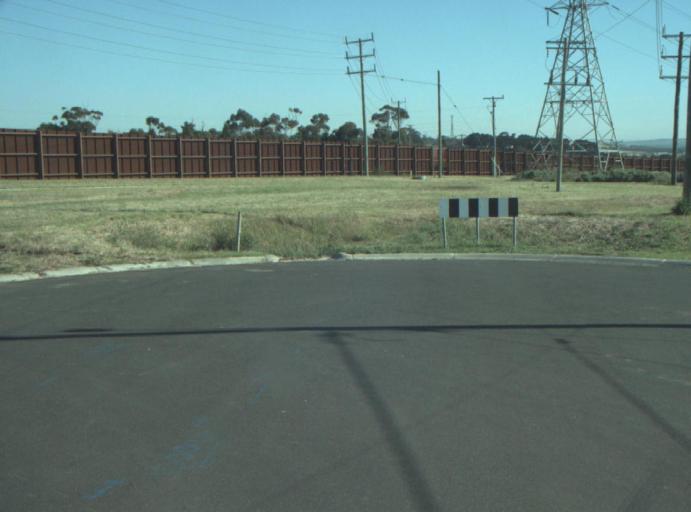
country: AU
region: Victoria
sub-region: Greater Geelong
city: Bell Post Hill
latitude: -38.0924
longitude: 144.3245
